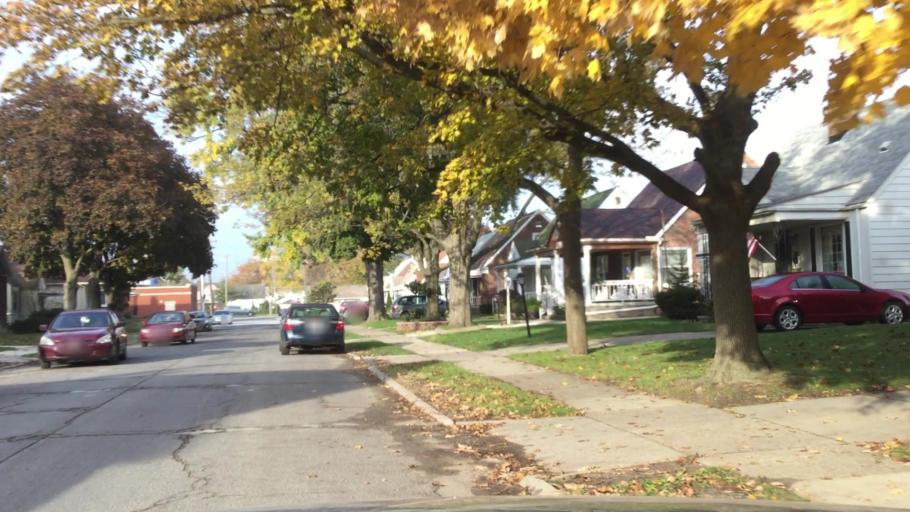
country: US
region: Michigan
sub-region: Wayne County
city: Dearborn
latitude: 42.3246
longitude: -83.1935
